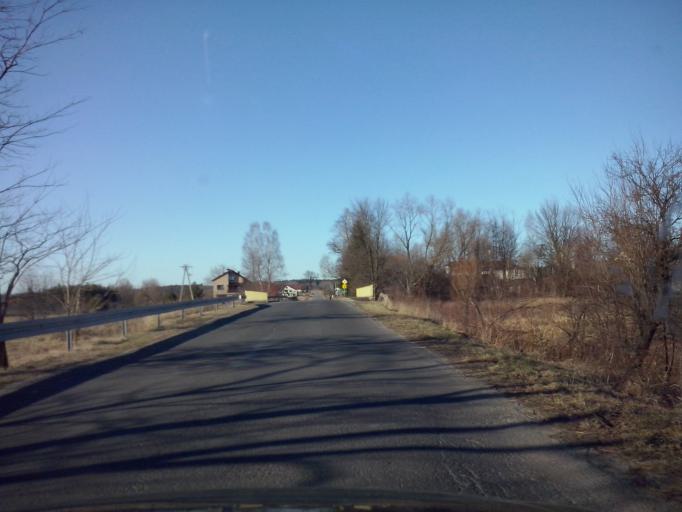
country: PL
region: Subcarpathian Voivodeship
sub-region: Powiat nizanski
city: Harasiuki
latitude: 50.5202
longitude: 22.4518
